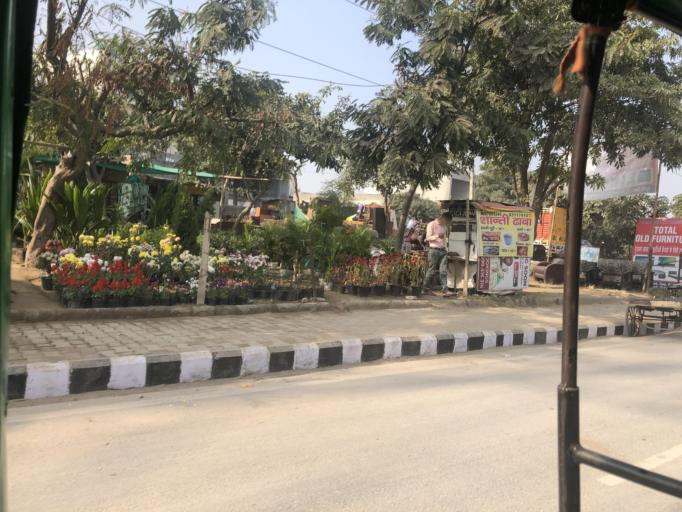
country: IN
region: Haryana
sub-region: Gurgaon
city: Gurgaon
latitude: 28.4378
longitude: 77.0898
